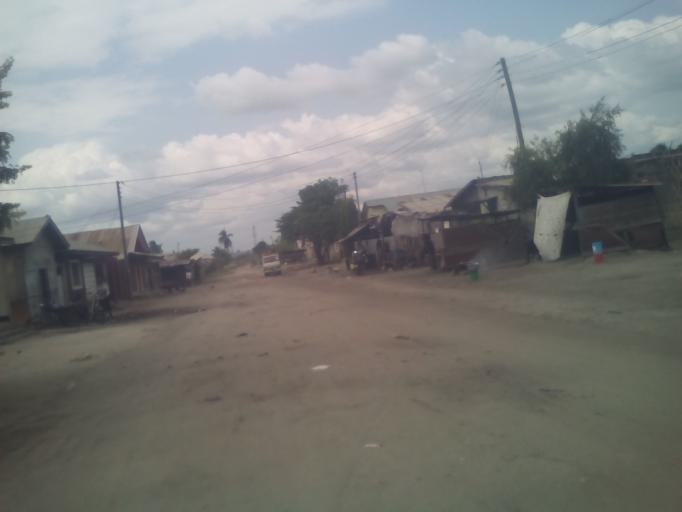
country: TZ
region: Dar es Salaam
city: Dar es Salaam
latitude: -6.8648
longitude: 39.2299
